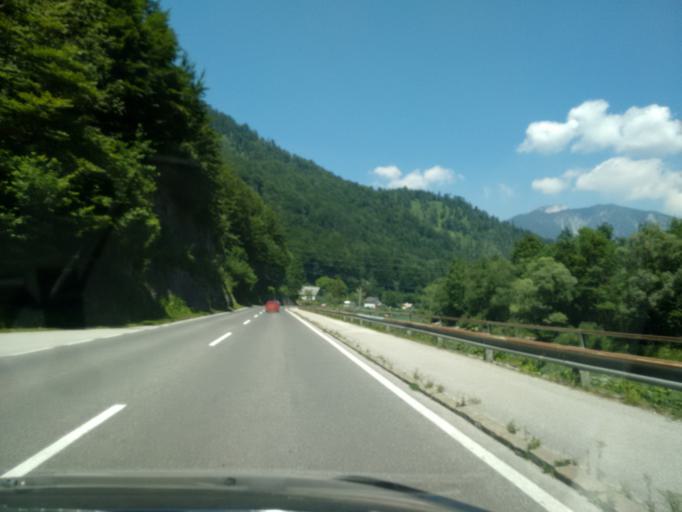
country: AT
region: Upper Austria
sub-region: Politischer Bezirk Gmunden
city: Bad Ischl
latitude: 47.7334
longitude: 13.6585
